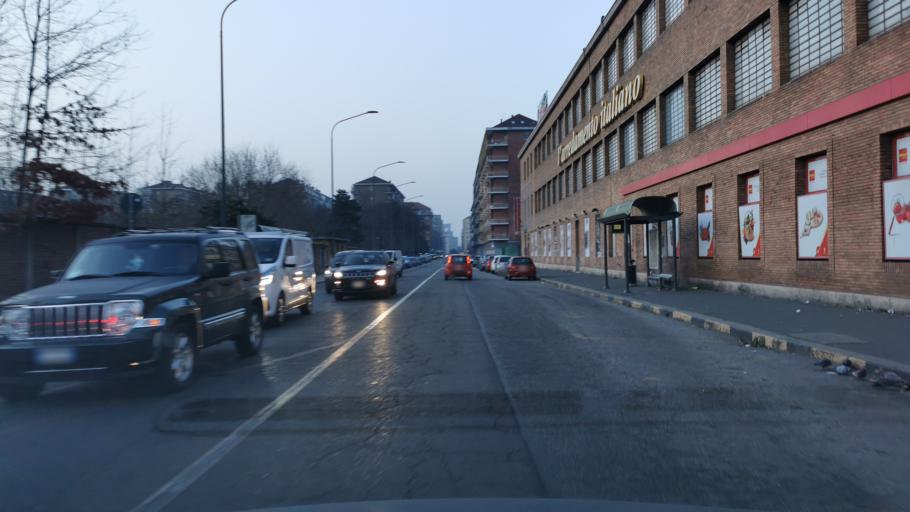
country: IT
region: Piedmont
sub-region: Provincia di Torino
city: Turin
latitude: 45.1043
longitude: 7.6729
